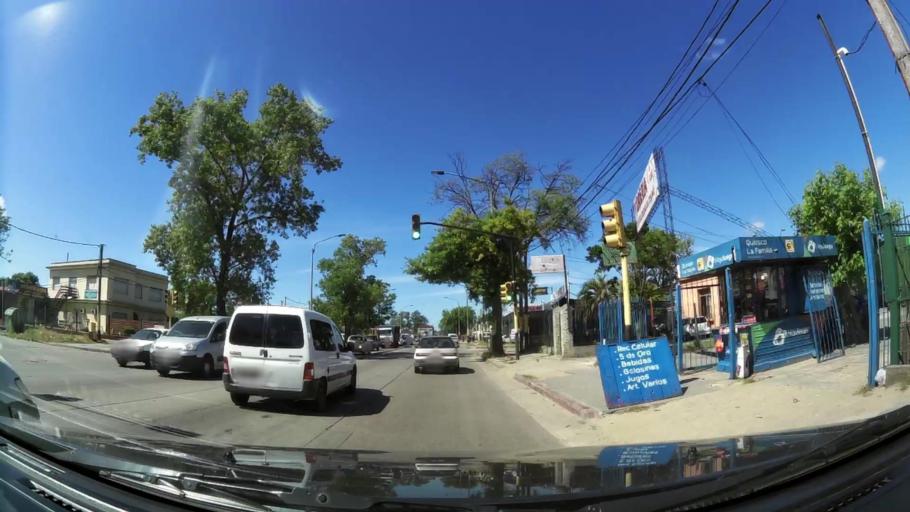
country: UY
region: Canelones
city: Paso de Carrasco
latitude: -34.8442
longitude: -56.1254
